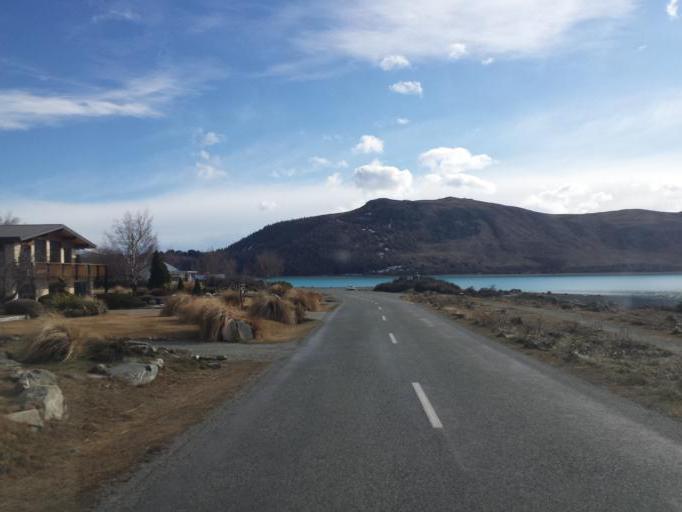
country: NZ
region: Canterbury
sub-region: Timaru District
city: Pleasant Point
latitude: -44.0046
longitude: 170.4853
